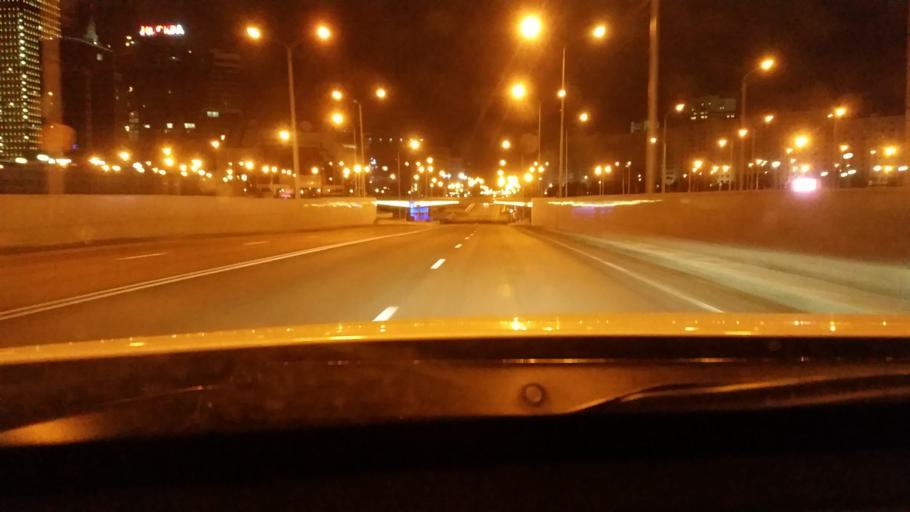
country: KZ
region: Astana Qalasy
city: Astana
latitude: 51.1197
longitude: 71.4357
